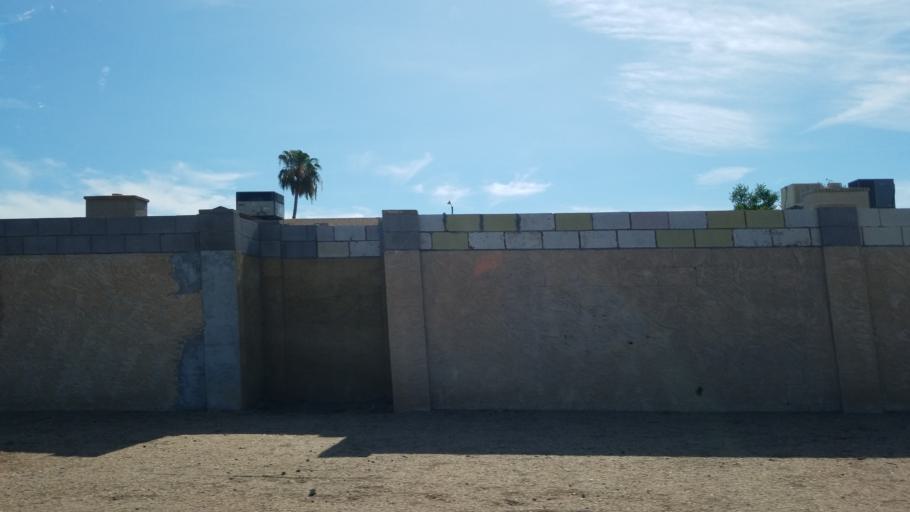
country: US
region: Arizona
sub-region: Maricopa County
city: Glendale
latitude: 33.6051
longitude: -112.1511
